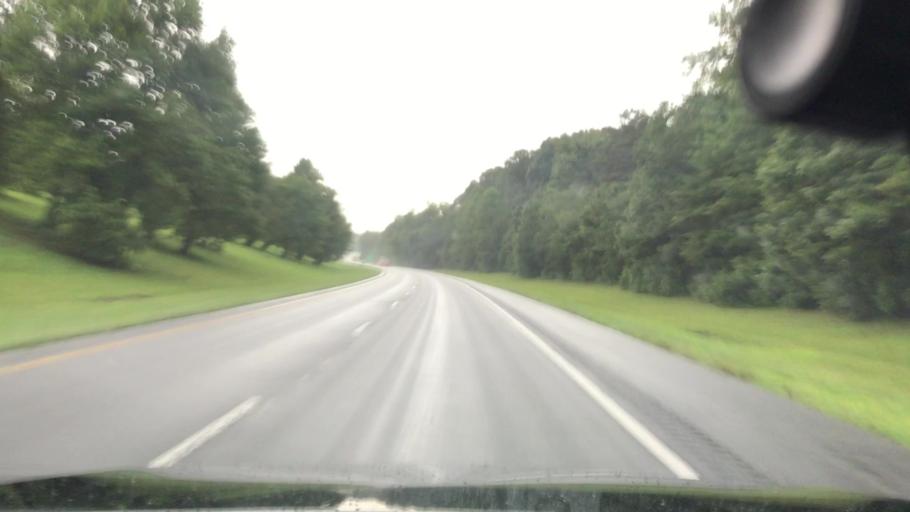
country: US
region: North Carolina
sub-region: Iredell County
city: Statesville
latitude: 35.9803
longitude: -80.8376
